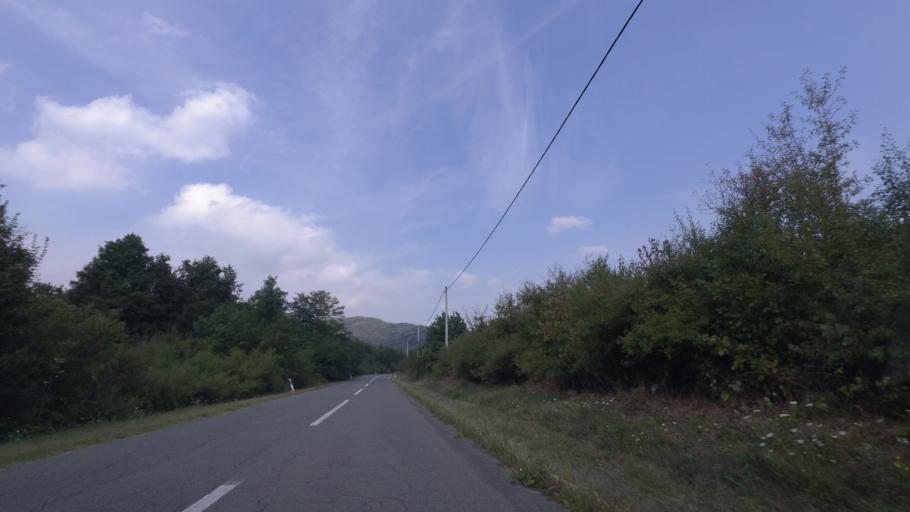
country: BA
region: Federation of Bosnia and Herzegovina
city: Zboriste
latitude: 45.1812
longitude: 16.1330
